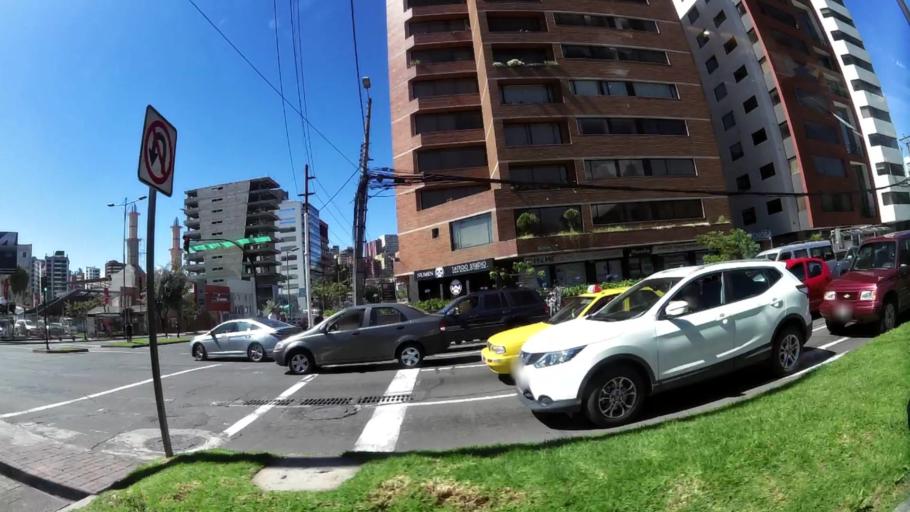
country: EC
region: Pichincha
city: Quito
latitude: -0.1890
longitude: -78.4829
